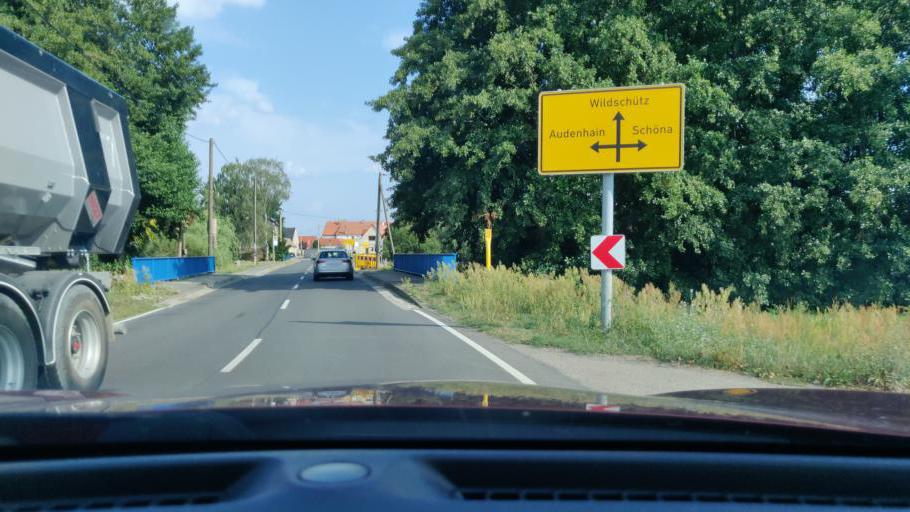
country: DE
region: Saxony
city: Mockrehna
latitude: 51.4933
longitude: 12.8284
